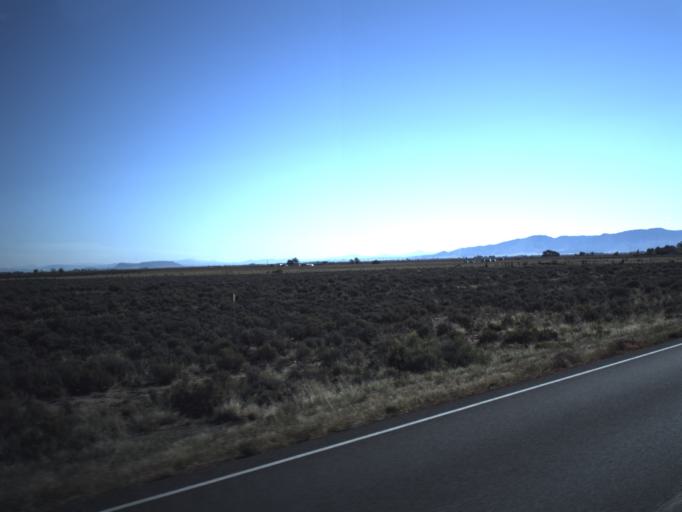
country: US
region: Utah
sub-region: Washington County
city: Enterprise
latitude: 37.7474
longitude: -113.7623
